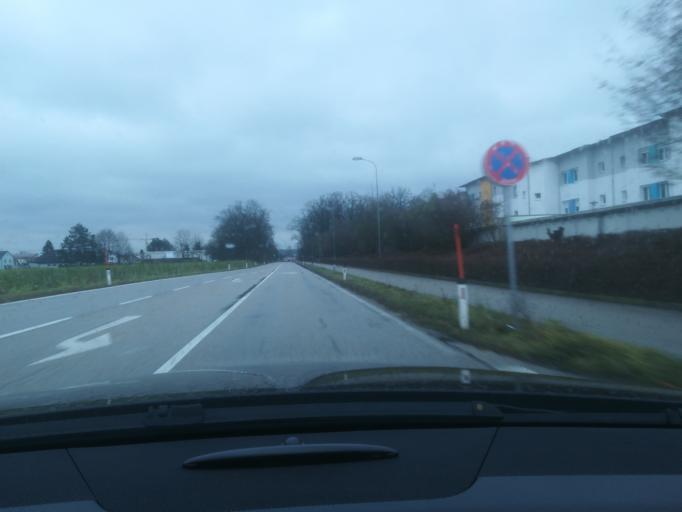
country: AT
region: Upper Austria
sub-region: Wels-Land
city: Marchtrenk
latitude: 48.1978
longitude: 14.1137
